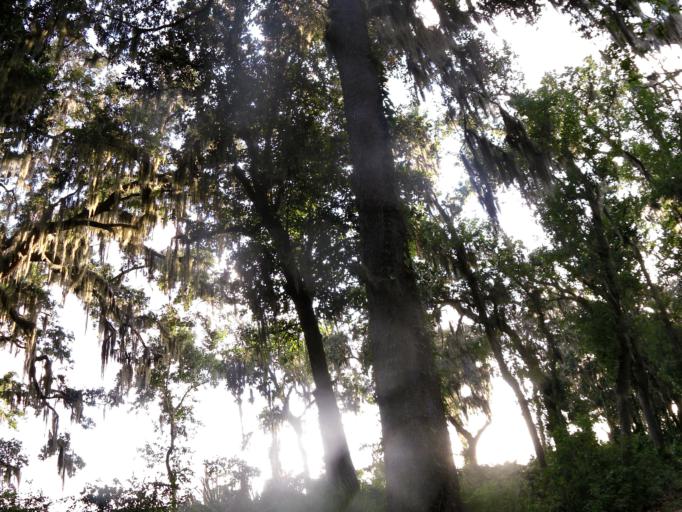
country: US
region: Florida
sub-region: Clay County
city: Green Cove Springs
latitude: 30.0234
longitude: -81.6442
